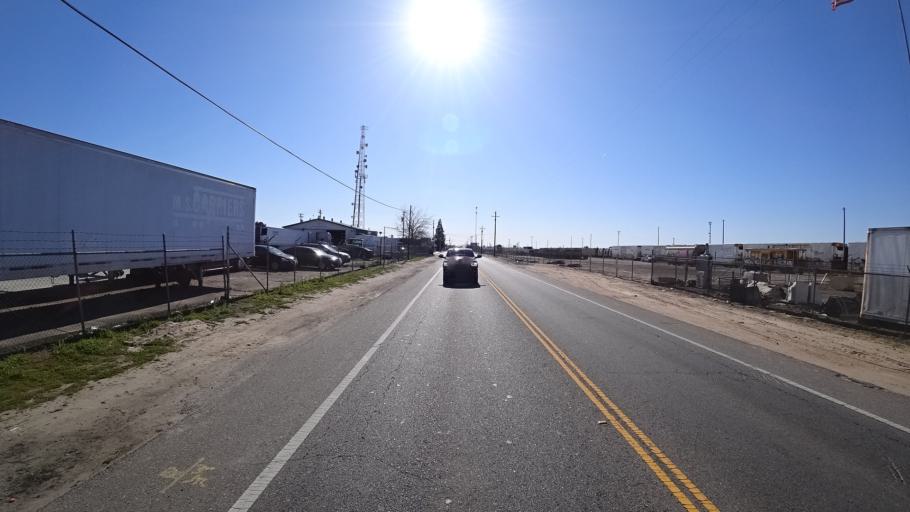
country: US
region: California
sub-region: Fresno County
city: West Park
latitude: 36.7848
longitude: -119.8481
